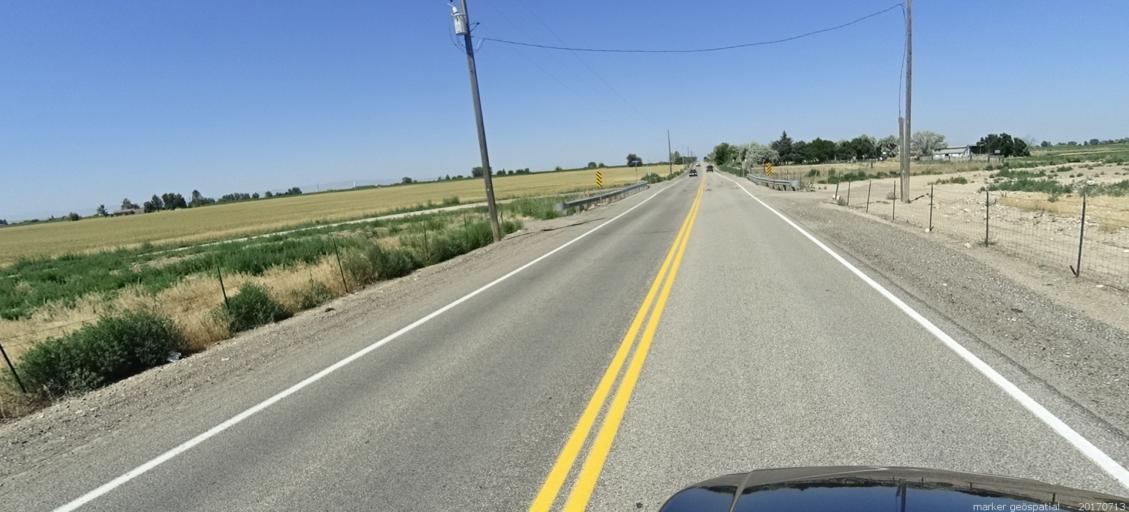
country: US
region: Idaho
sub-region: Ada County
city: Kuna
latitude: 43.5320
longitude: -116.4025
